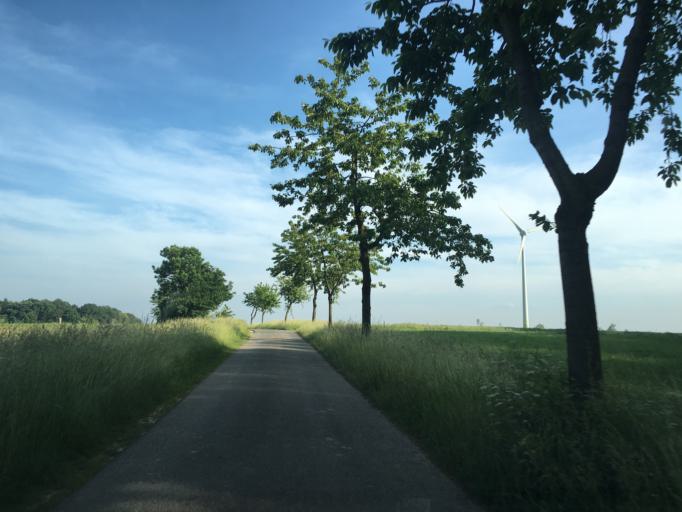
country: DE
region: North Rhine-Westphalia
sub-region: Regierungsbezirk Munster
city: Altenberge
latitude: 52.0137
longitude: 7.5346
